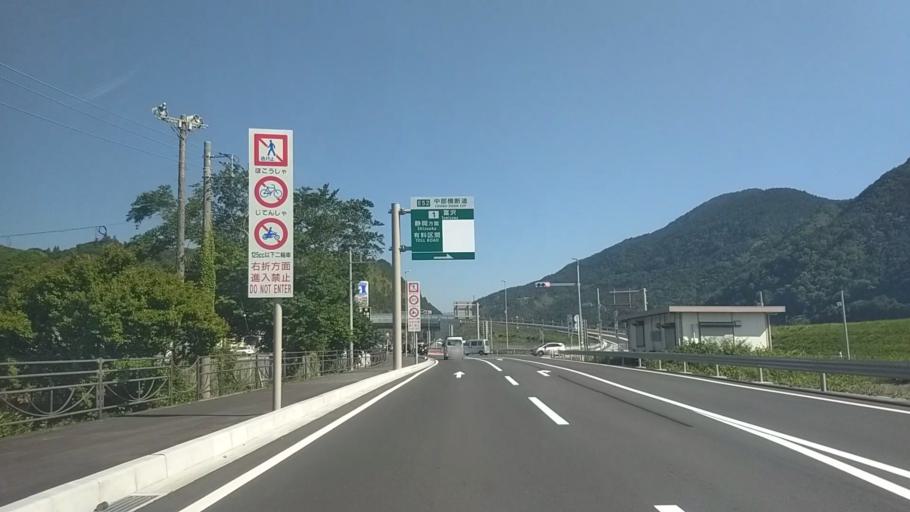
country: JP
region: Shizuoka
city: Fujinomiya
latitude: 35.2488
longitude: 138.4810
